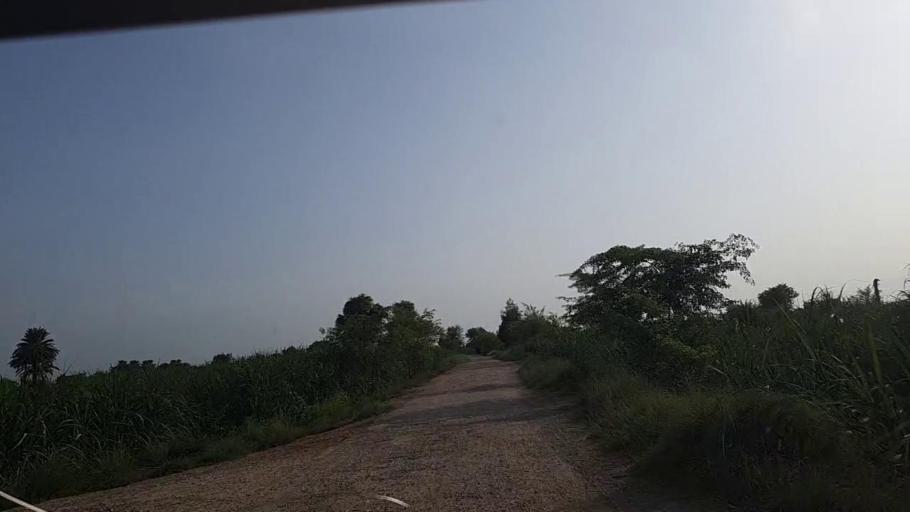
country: PK
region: Sindh
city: Ghotki
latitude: 27.9844
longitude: 69.2542
